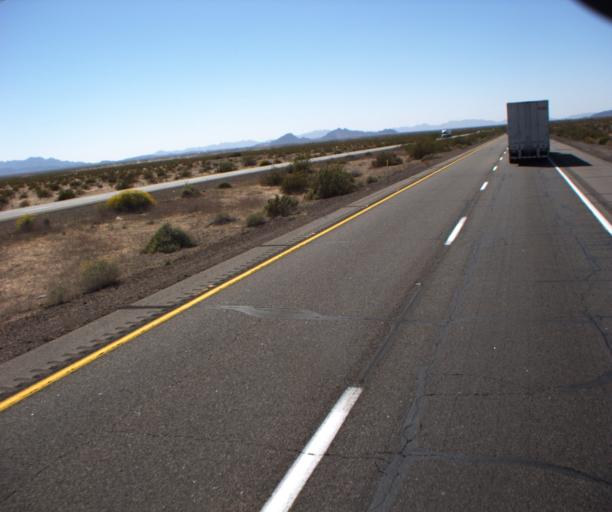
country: US
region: Arizona
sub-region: Yuma County
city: Wellton
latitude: 32.7115
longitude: -113.8362
